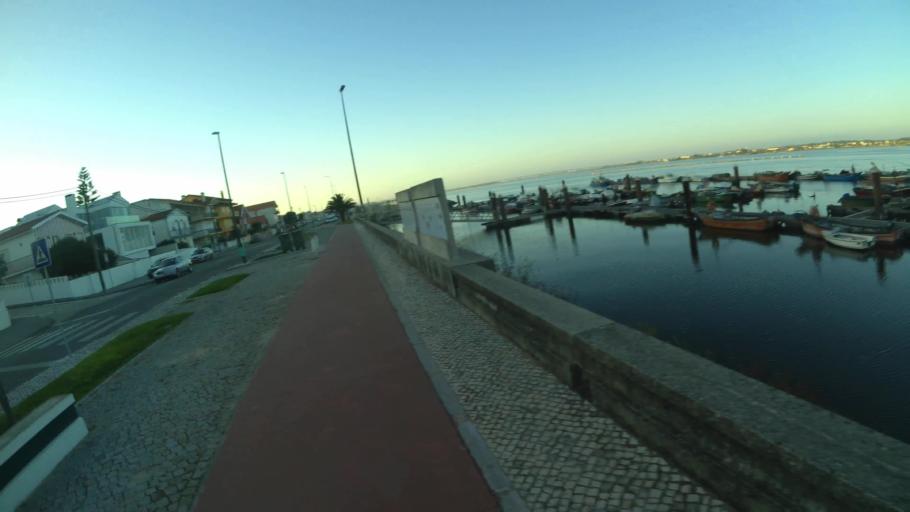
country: PT
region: Aveiro
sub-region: Ilhavo
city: Gafanha da Encarnacao
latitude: 40.6087
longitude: -8.7488
